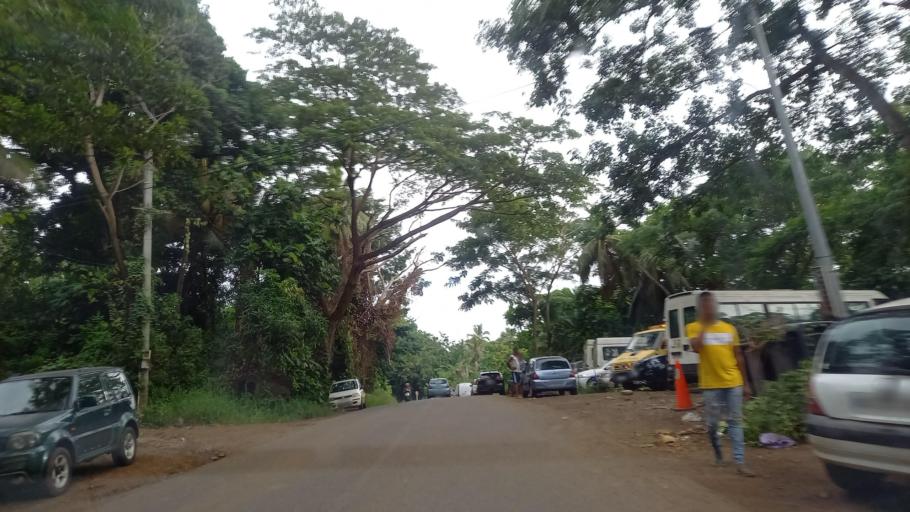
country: YT
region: Sada
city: Sada
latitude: -12.8656
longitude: 45.1137
